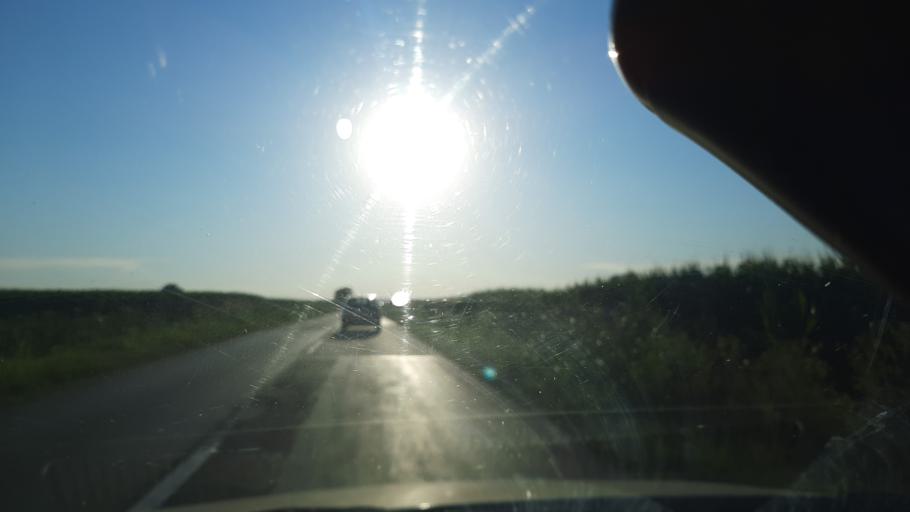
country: RS
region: Central Serbia
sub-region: Branicevski Okrug
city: Malo Crnice
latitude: 44.5815
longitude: 21.3127
